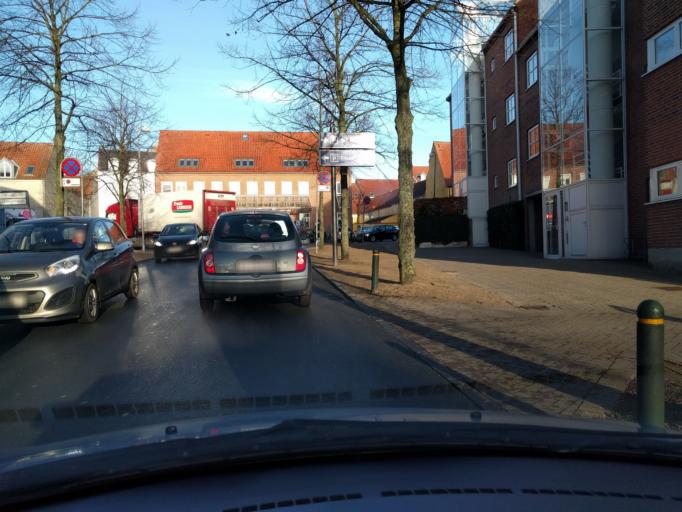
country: DK
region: South Denmark
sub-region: Odense Kommune
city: Odense
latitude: 55.3934
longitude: 10.3831
